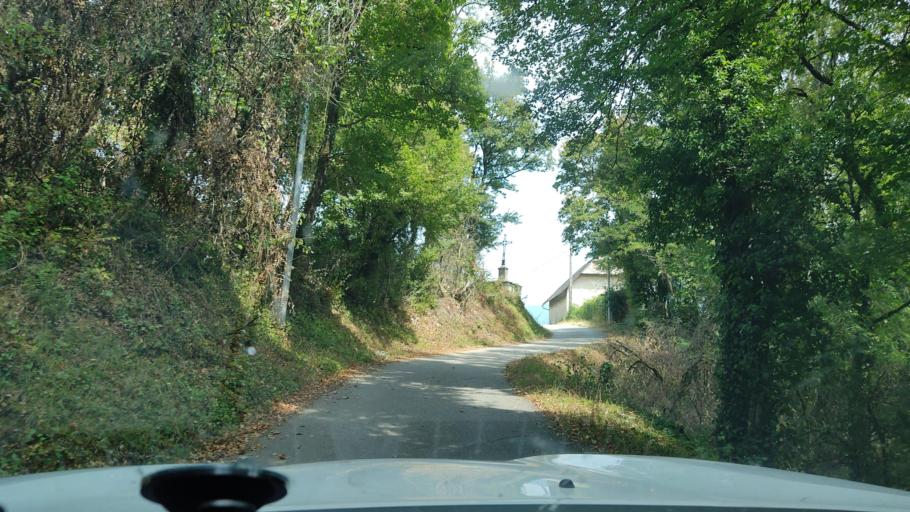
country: FR
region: Rhone-Alpes
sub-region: Departement de la Savoie
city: Saint-Baldoph
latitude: 45.5129
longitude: 5.9541
